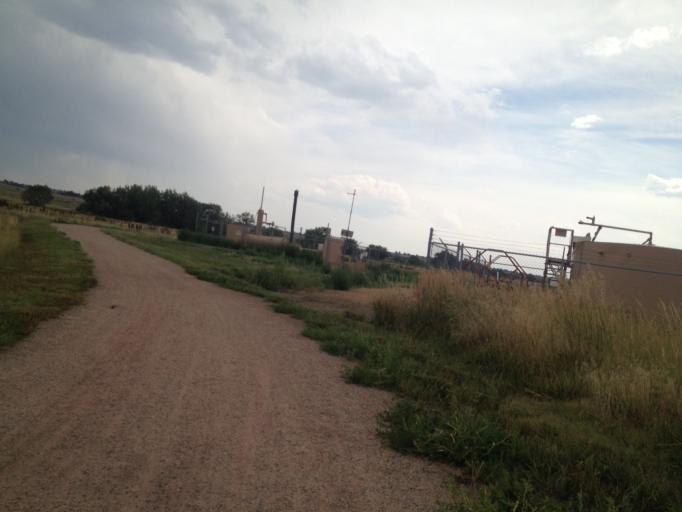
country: US
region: Colorado
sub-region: Boulder County
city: Lafayette
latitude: 39.9688
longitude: -105.0826
